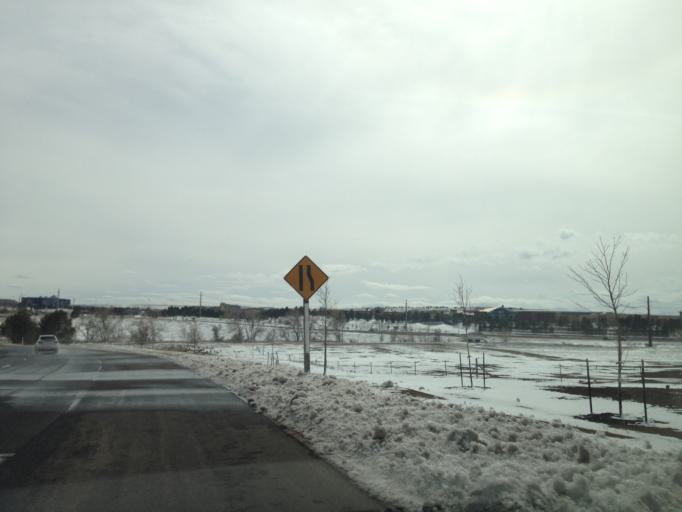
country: US
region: Colorado
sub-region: Boulder County
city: Louisville
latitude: 39.9401
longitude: -105.1280
